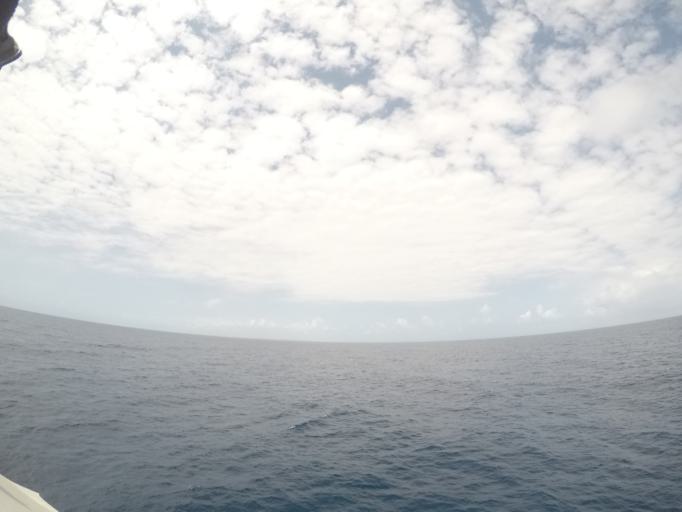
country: TZ
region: Zanzibar North
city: Nungwi
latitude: -5.6039
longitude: 39.3389
